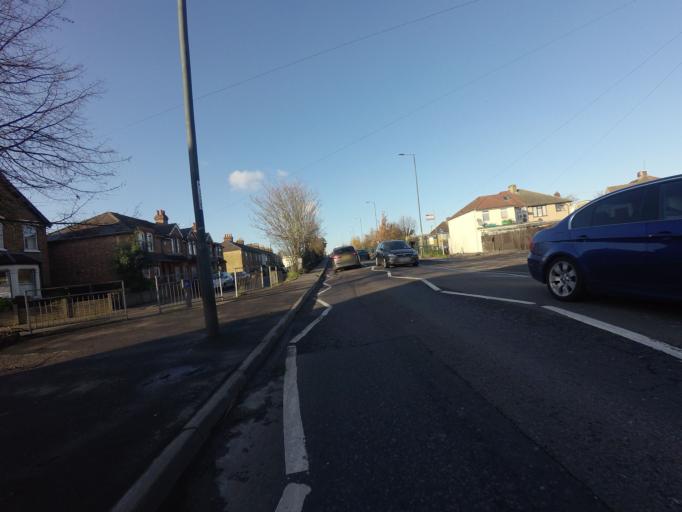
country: GB
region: England
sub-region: Greater London
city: Feltham
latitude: 51.4479
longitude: -0.4022
